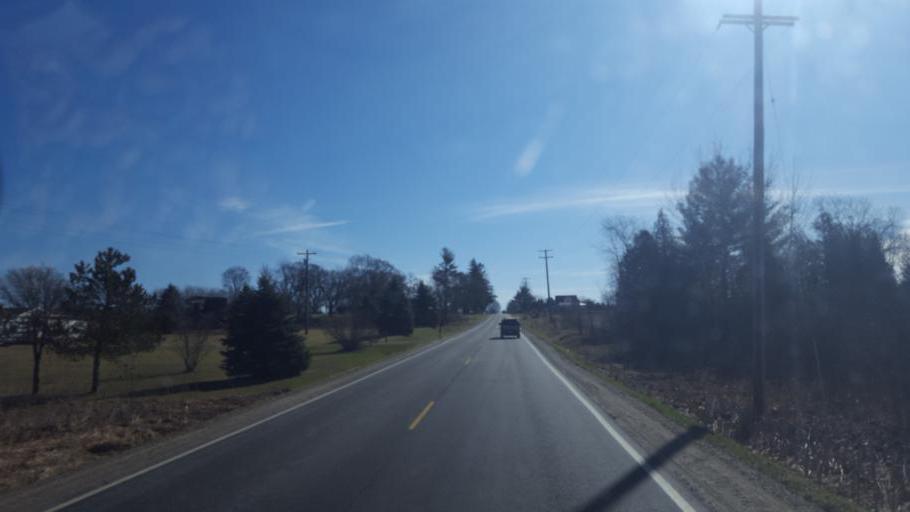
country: US
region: Michigan
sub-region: Montcalm County
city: Edmore
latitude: 43.5239
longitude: -85.0106
